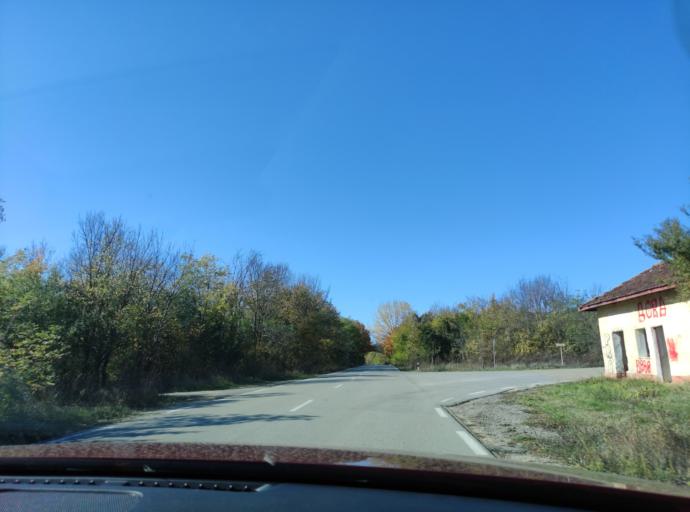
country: BG
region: Montana
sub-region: Obshtina Chiprovtsi
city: Chiprovtsi
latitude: 43.4275
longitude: 23.0039
